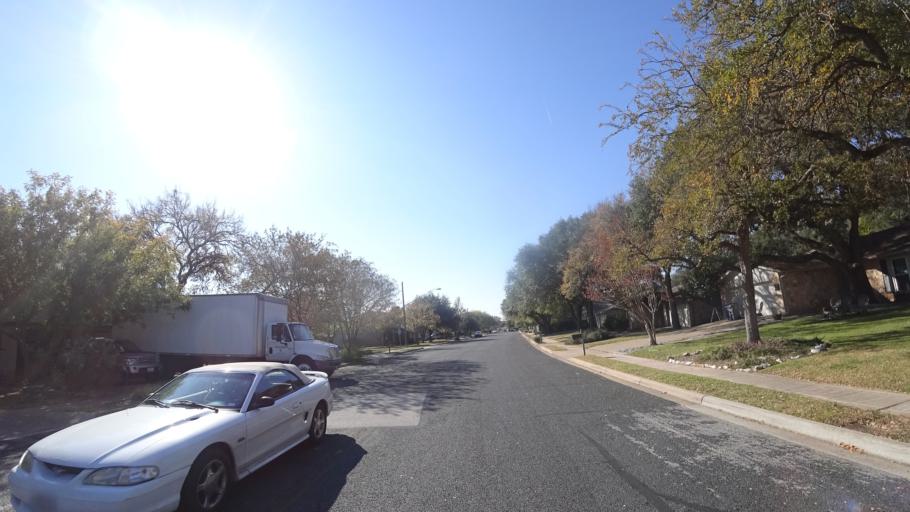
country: US
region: Texas
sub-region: Travis County
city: Barton Creek
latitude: 30.2321
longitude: -97.8490
